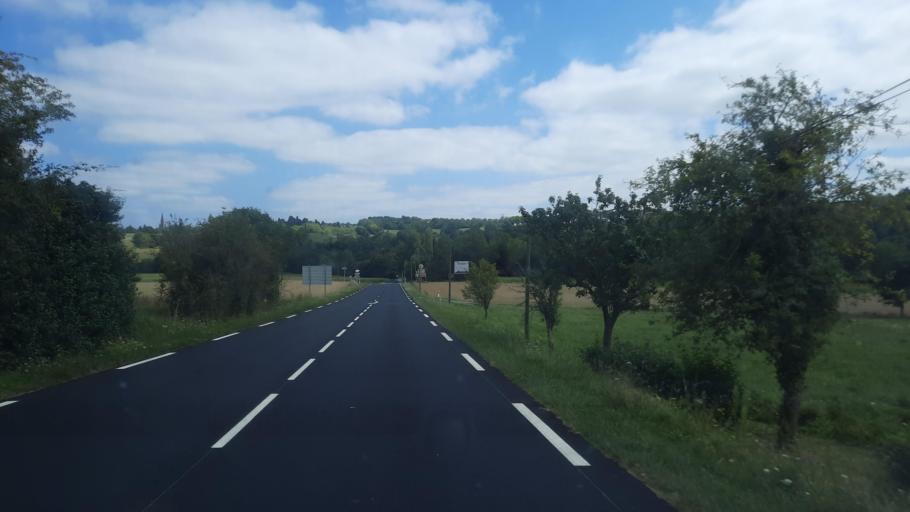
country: FR
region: Midi-Pyrenees
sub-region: Departement de la Haute-Garonne
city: Boulogne-sur-Gesse
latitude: 43.2949
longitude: 0.6260
